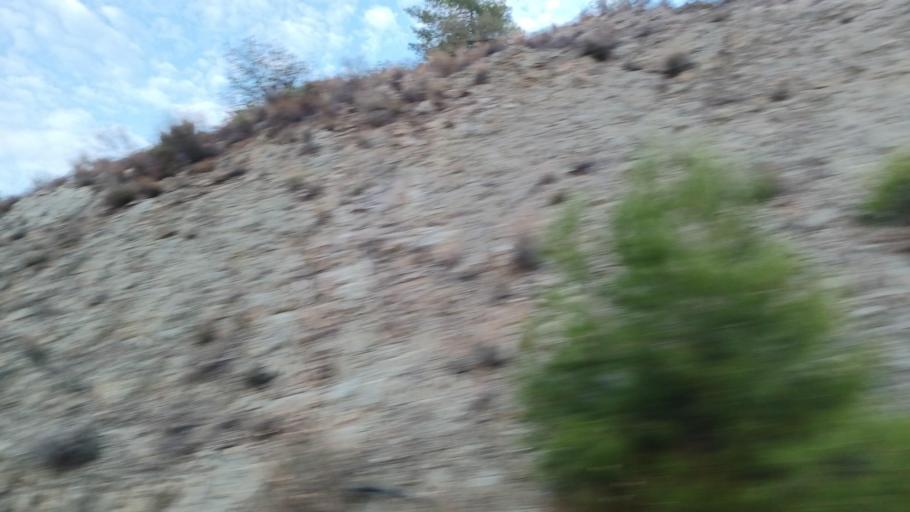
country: CY
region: Limassol
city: Pelendri
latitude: 34.8443
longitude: 32.9495
